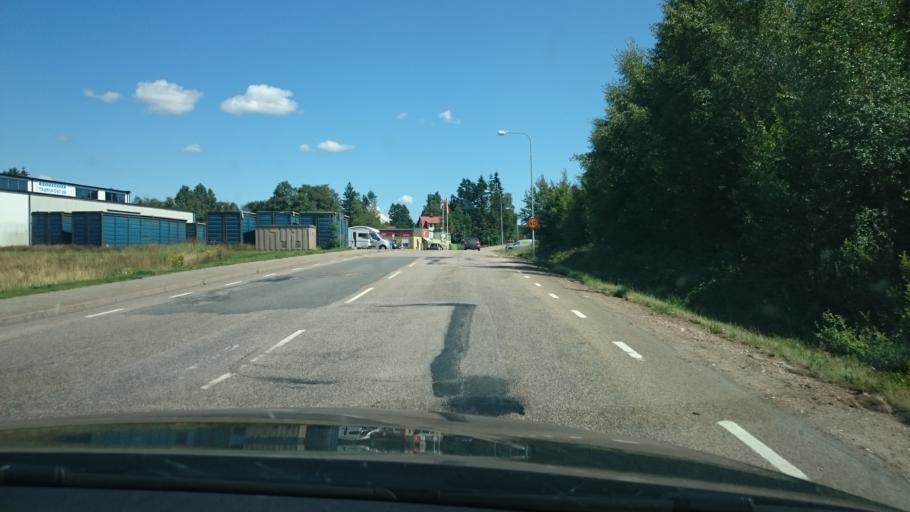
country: SE
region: Halland
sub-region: Hylte Kommun
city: Hyltebruk
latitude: 56.9875
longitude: 13.2341
